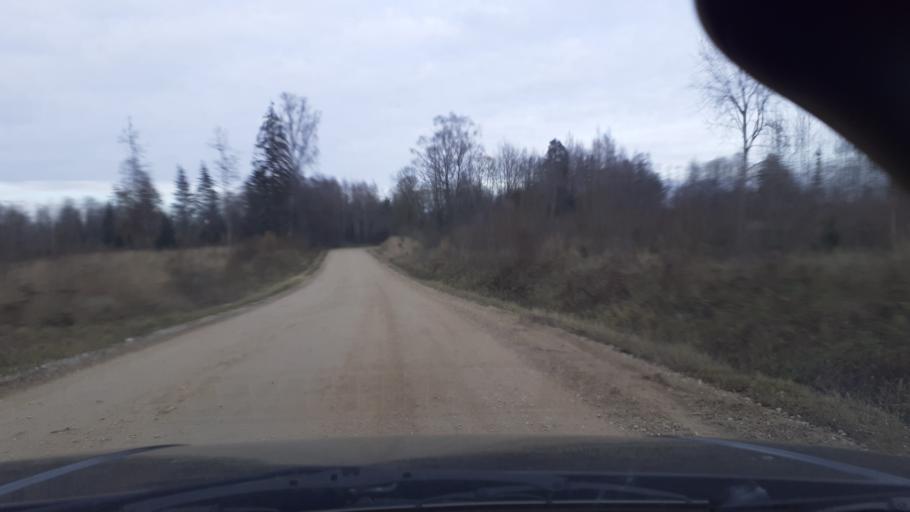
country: LV
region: Alsunga
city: Alsunga
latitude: 56.9652
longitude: 21.6549
